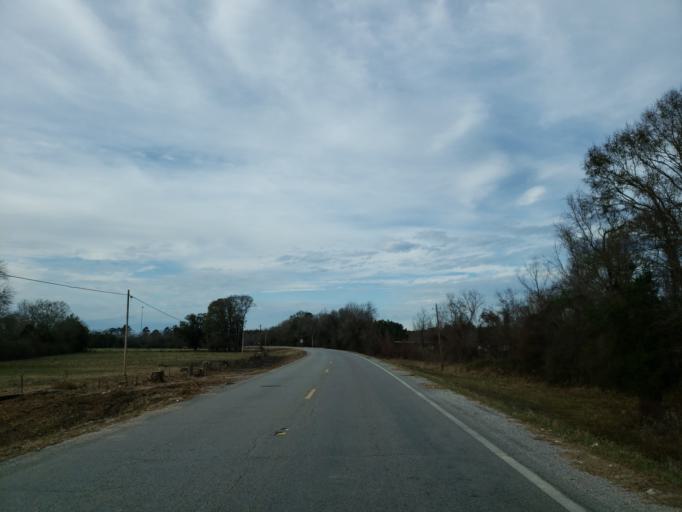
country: US
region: Mississippi
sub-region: Clarke County
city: Quitman
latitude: 31.8687
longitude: -88.7025
